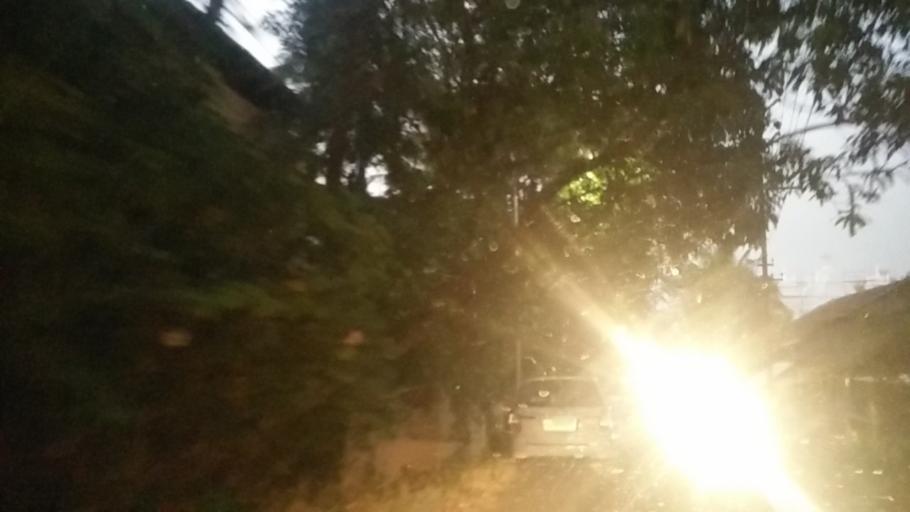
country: IN
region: Goa
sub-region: South Goa
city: Madgaon
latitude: 15.2823
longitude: 73.9673
